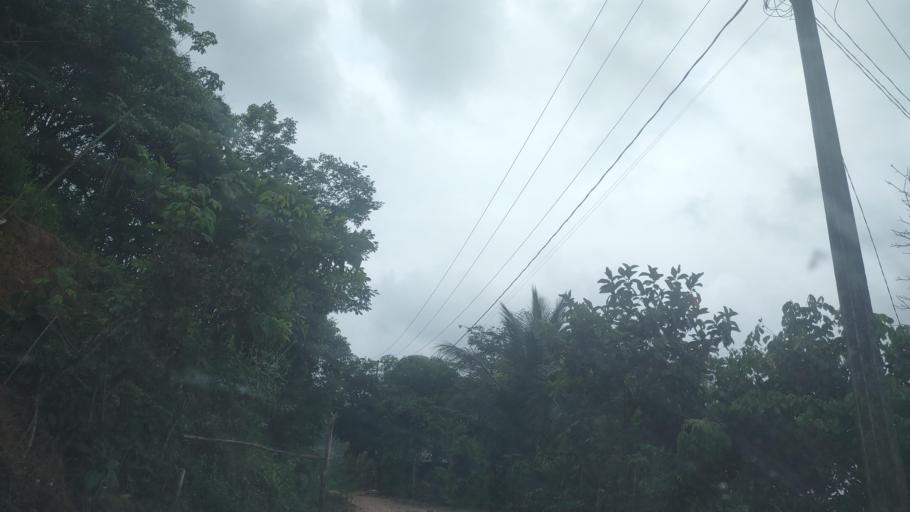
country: MX
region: Tabasco
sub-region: Huimanguillo
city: Francisco Rueda
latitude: 17.4449
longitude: -94.0246
